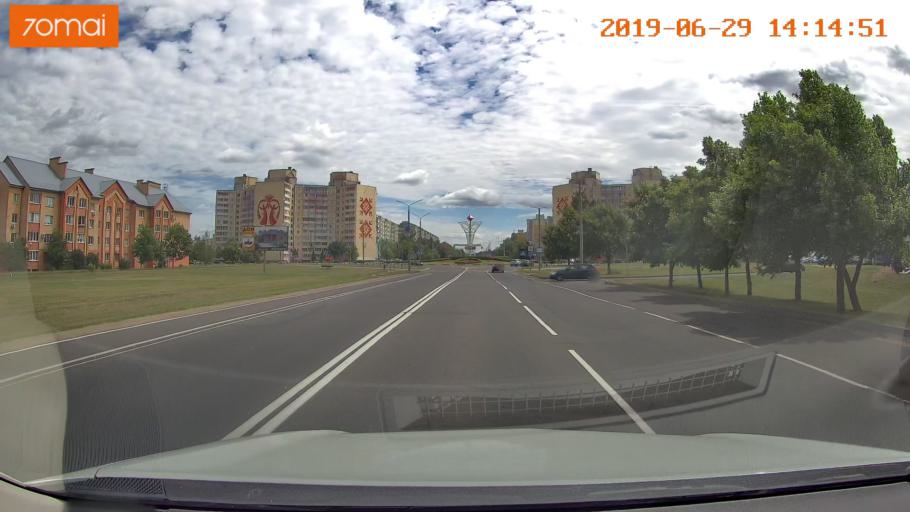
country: BY
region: Minsk
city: Salihorsk
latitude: 52.7930
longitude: 27.5184
